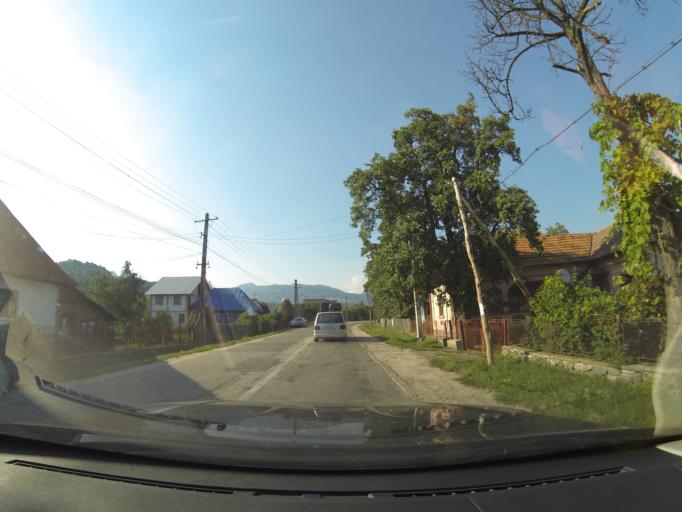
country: RO
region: Arges
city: Poenari
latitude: 45.3155
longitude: 24.6438
